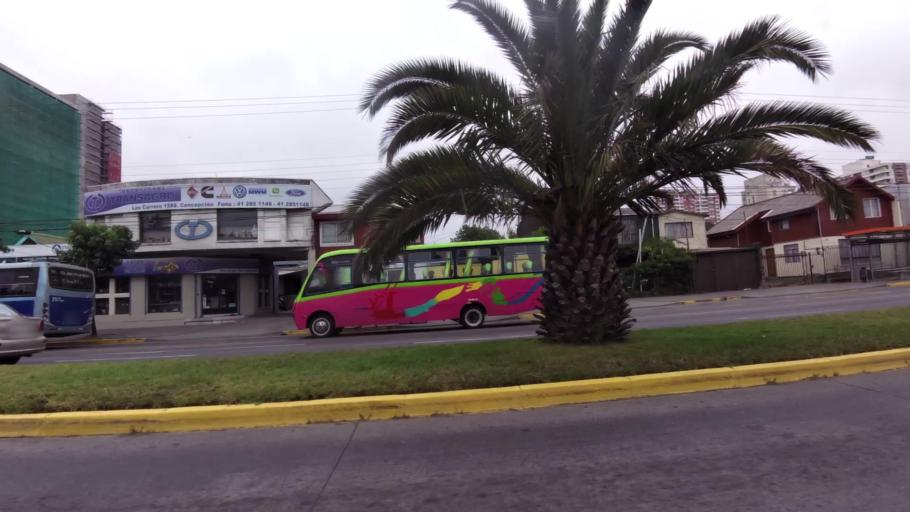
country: CL
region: Biobio
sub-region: Provincia de Concepcion
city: Concepcion
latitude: -36.8186
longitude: -73.0406
